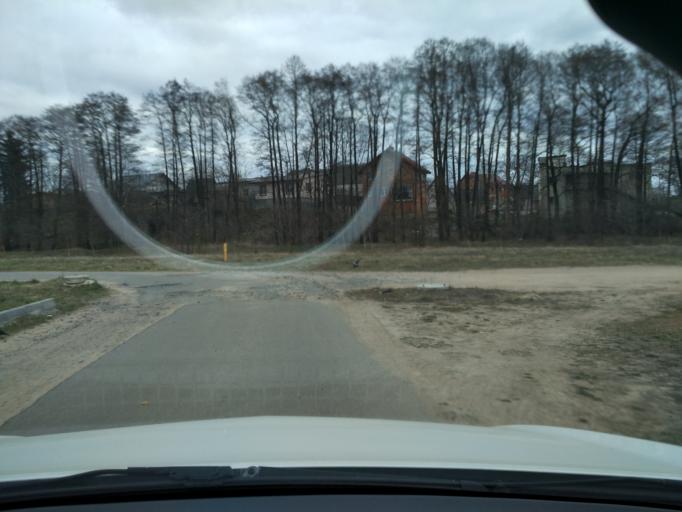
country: BY
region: Minsk
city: Bal'shavik
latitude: 53.9664
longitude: 27.5865
